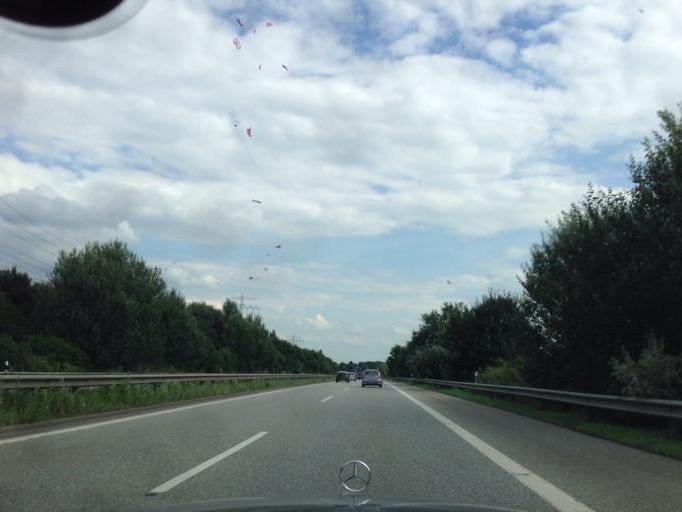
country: DE
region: Hamburg
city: Rothenburgsort
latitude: 53.4963
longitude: 10.0960
